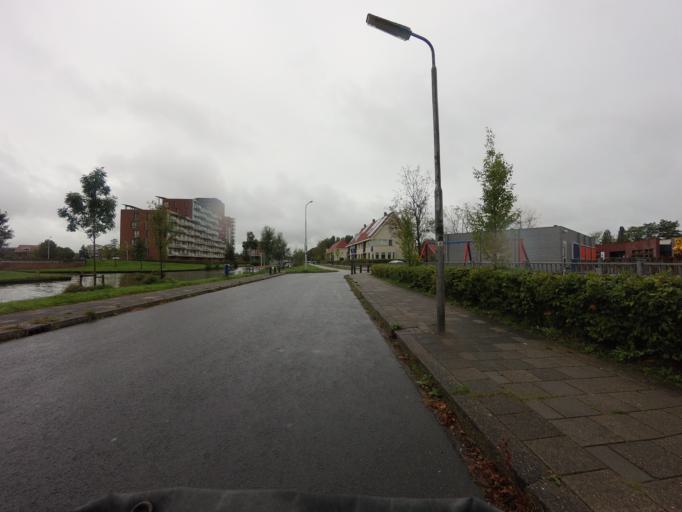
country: NL
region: Friesland
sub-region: Gemeente Leeuwarden
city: Bilgaard
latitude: 53.2153
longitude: 5.8051
